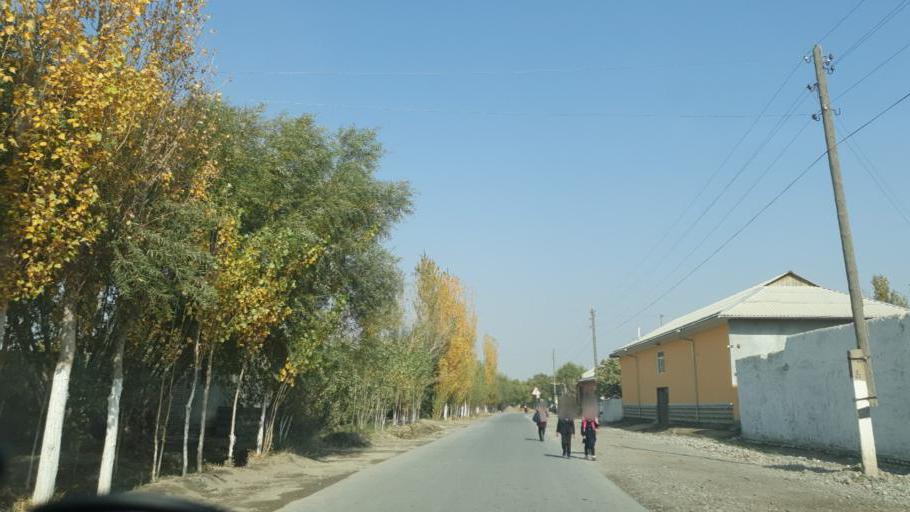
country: UZ
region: Fergana
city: Beshariq
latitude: 40.4935
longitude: 70.6213
